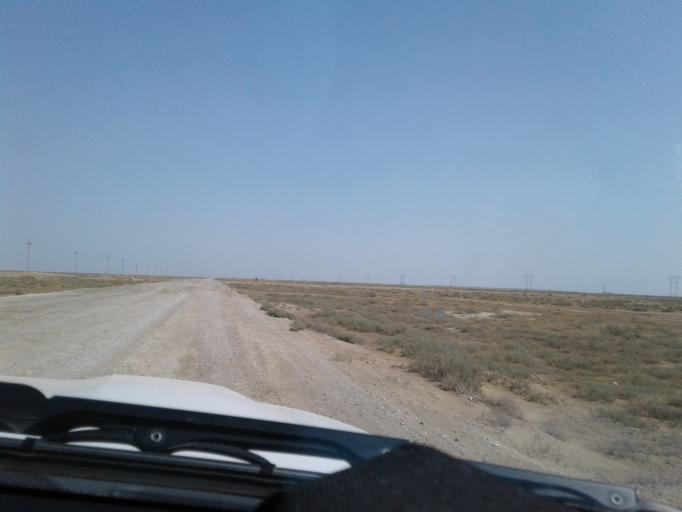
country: IR
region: Golestan
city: Gomishan
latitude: 37.7844
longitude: 53.9167
